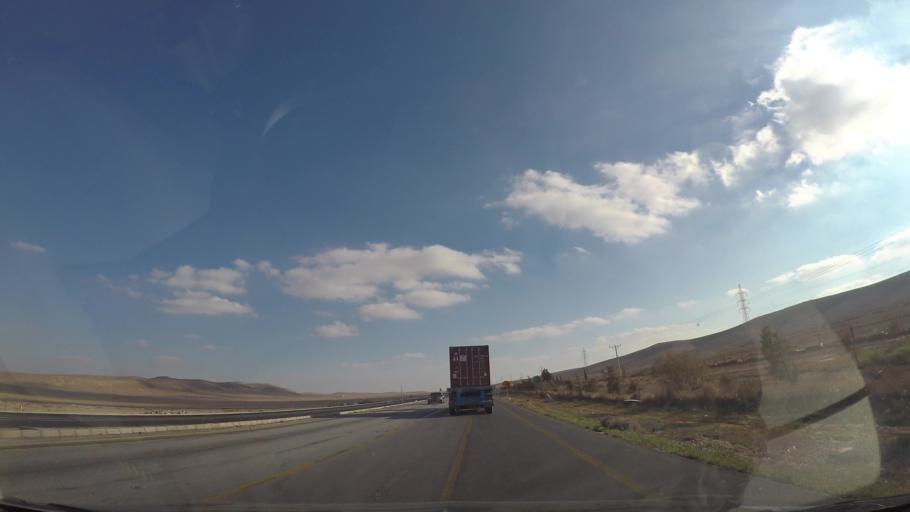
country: JO
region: Karak
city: Adir
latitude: 31.1900
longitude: 36.0178
